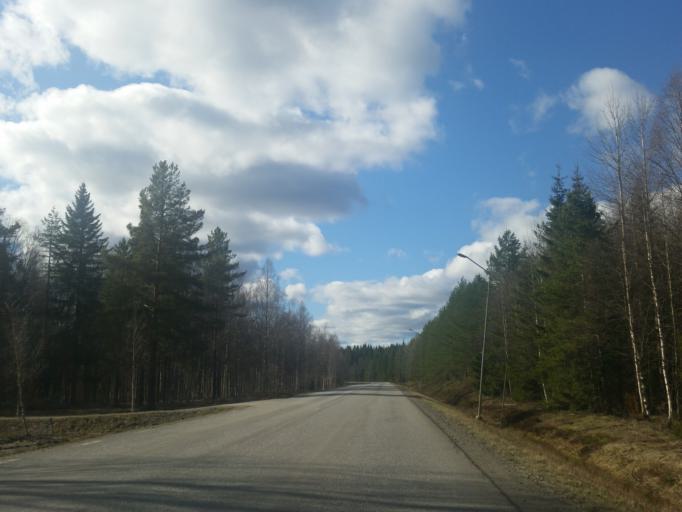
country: SE
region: Vaesterbotten
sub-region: Robertsfors Kommun
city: Robertsfors
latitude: 64.1988
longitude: 20.8347
